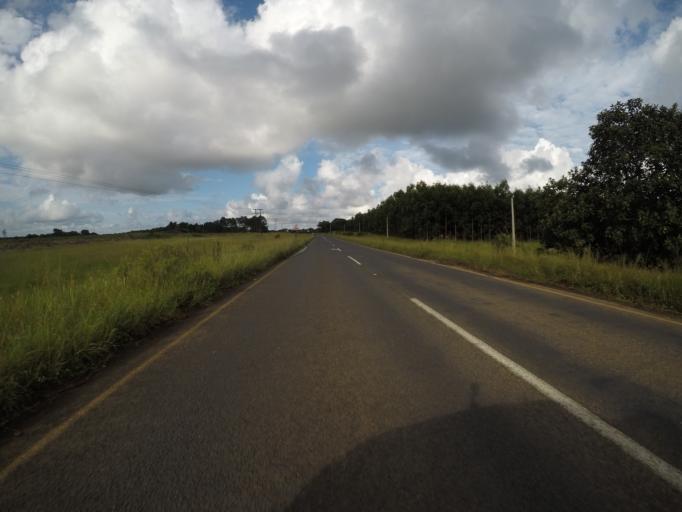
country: ZA
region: KwaZulu-Natal
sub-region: uMkhanyakude District Municipality
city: Mtubatuba
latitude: -28.3802
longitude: 32.2467
